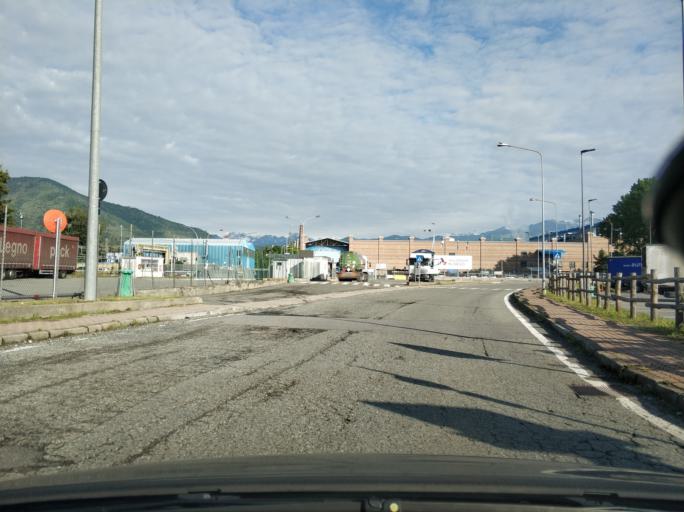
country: IT
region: Piedmont
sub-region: Provincia di Torino
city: Mathi
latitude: 45.2520
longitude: 7.5375
